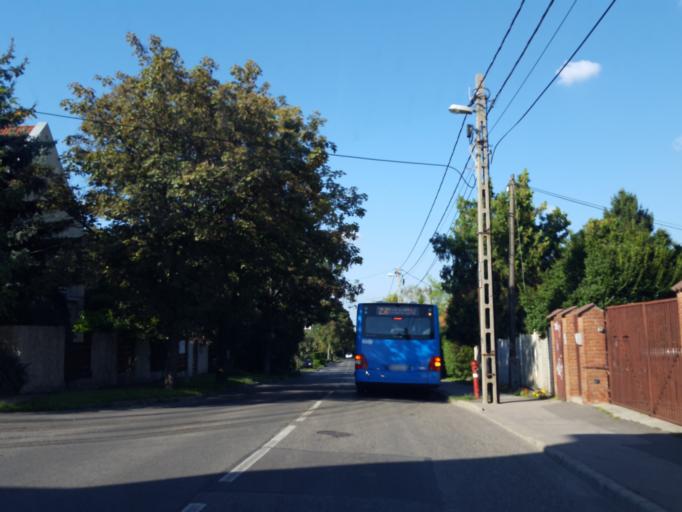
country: HU
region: Budapest
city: Budapest XXII. keruelet
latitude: 47.4469
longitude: 19.0141
